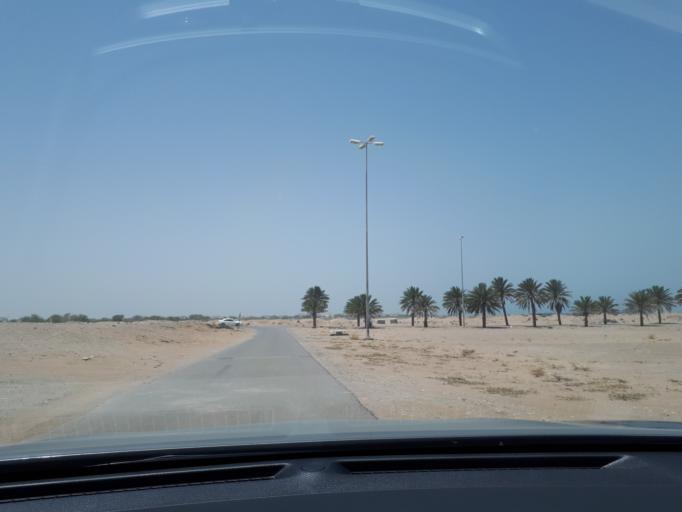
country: OM
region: Muhafazat Masqat
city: As Sib al Jadidah
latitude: 23.6310
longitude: 58.2604
